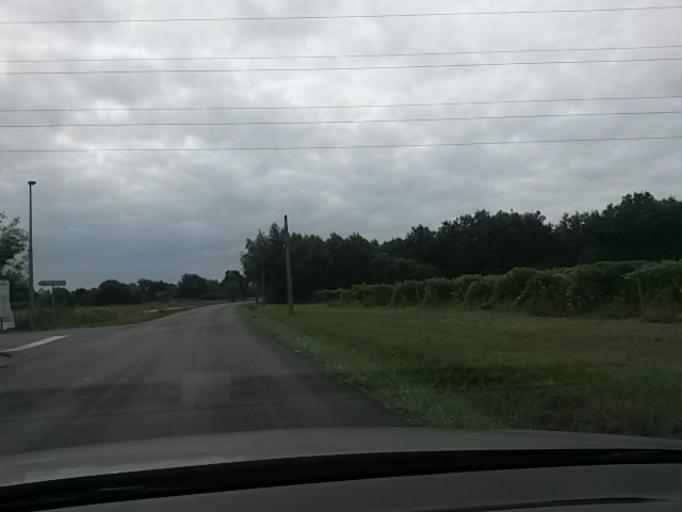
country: FR
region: Poitou-Charentes
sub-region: Departement de la Charente-Maritime
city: Dolus-d'Oleron
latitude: 45.8861
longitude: -1.2408
